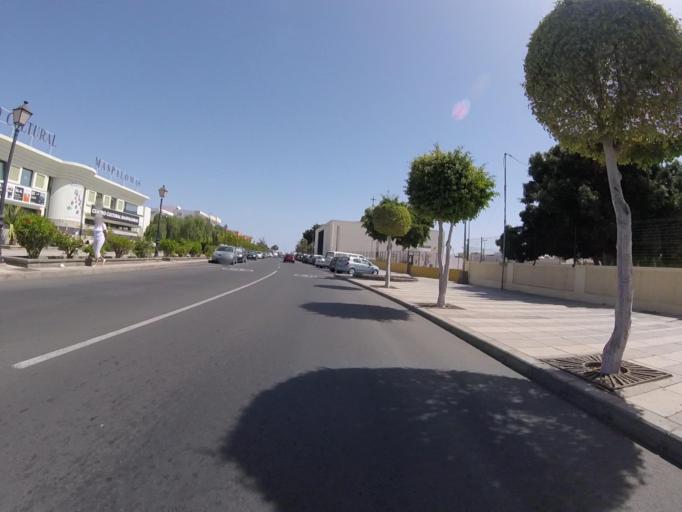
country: ES
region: Canary Islands
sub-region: Provincia de Las Palmas
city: Maspalomas
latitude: 27.7663
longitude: -15.5814
